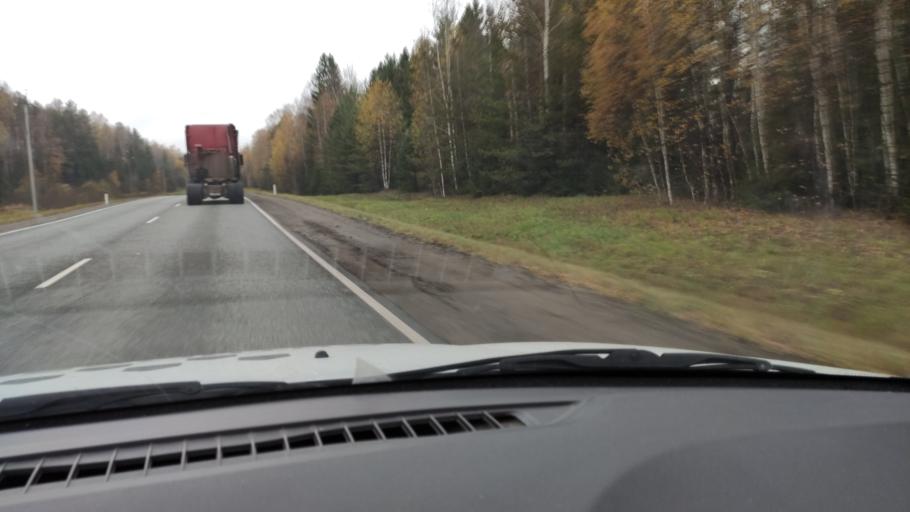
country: RU
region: Kirov
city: Belaya Kholunitsa
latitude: 58.8488
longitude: 50.7184
